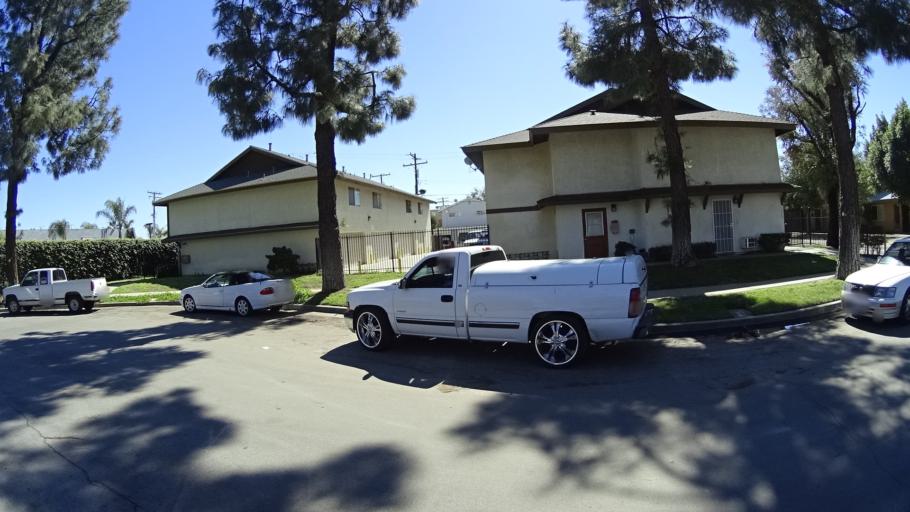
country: US
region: California
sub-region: Orange County
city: Anaheim
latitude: 33.8238
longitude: -117.9173
